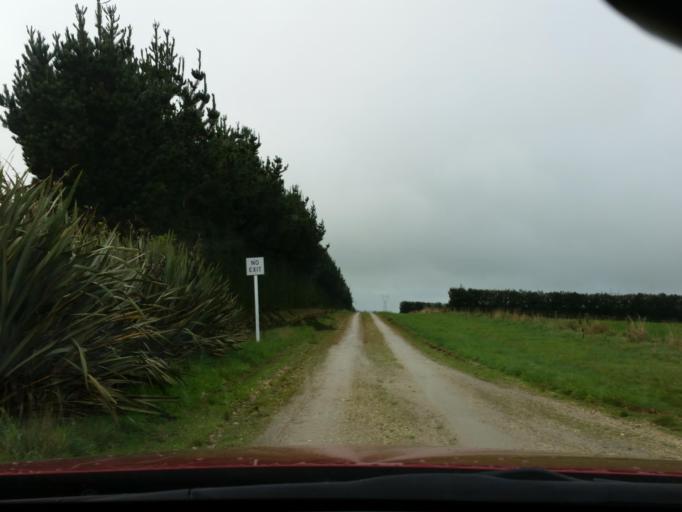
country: NZ
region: Southland
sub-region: Invercargill City
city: Invercargill
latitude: -46.2849
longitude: 168.5696
